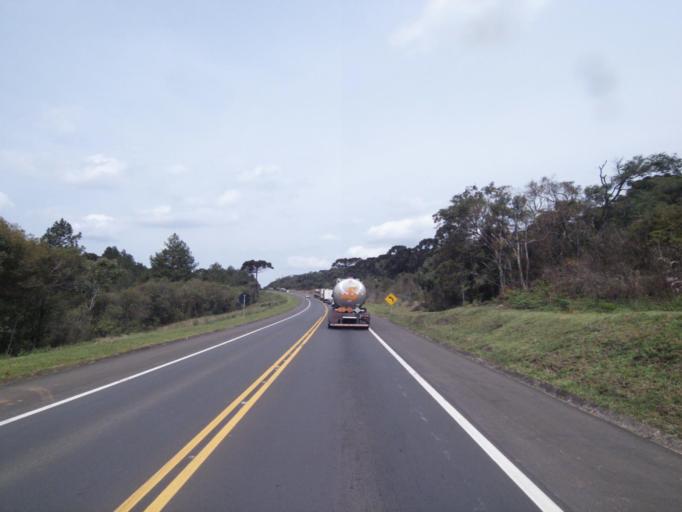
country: BR
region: Parana
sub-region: Irati
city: Irati
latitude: -25.4654
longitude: -50.4148
